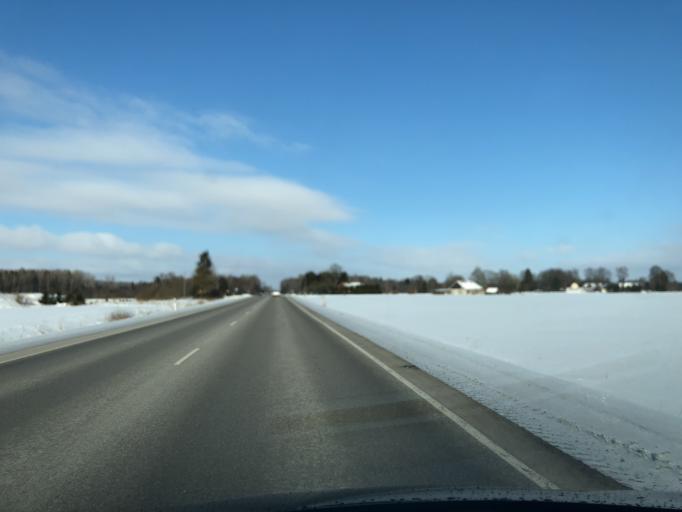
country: EE
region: Jaervamaa
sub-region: Paide linn
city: Paide
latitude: 58.8035
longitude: 25.7579
